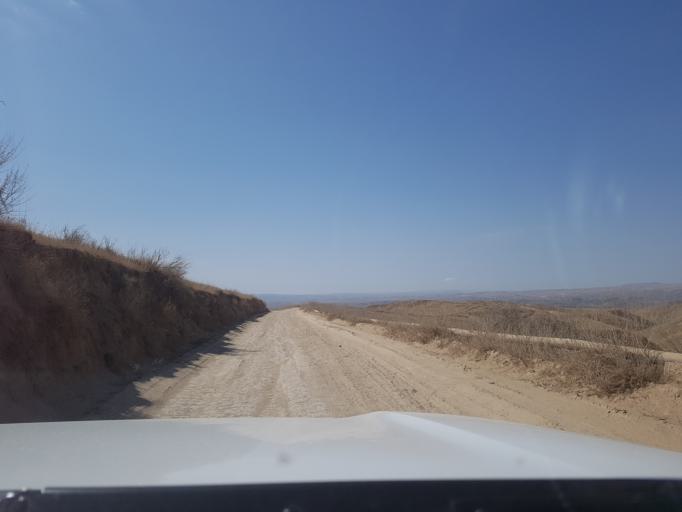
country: TM
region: Ahal
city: Baharly
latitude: 38.2690
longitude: 56.8930
